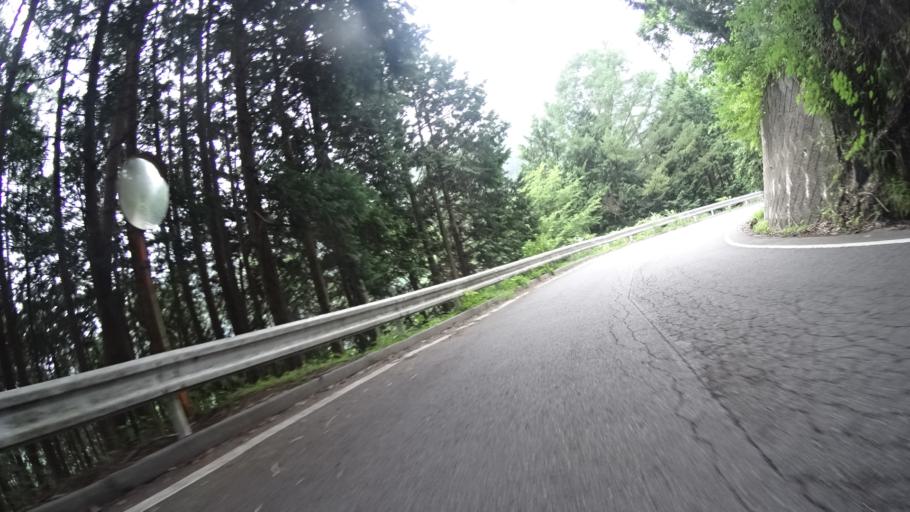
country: JP
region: Yamanashi
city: Enzan
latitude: 35.7914
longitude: 138.6848
